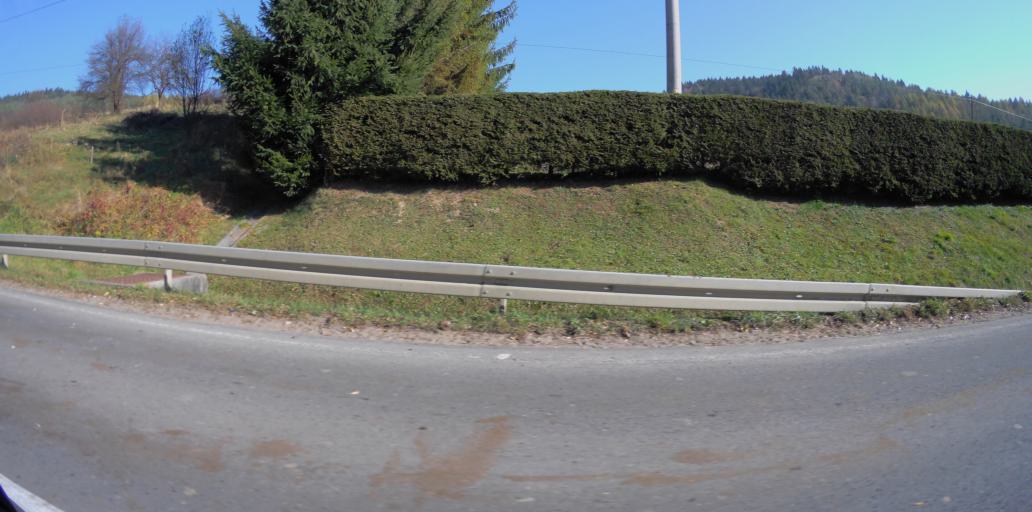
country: PL
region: Subcarpathian Voivodeship
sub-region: Powiat bieszczadzki
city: Ustrzyki Dolne
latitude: 49.4851
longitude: 22.6618
